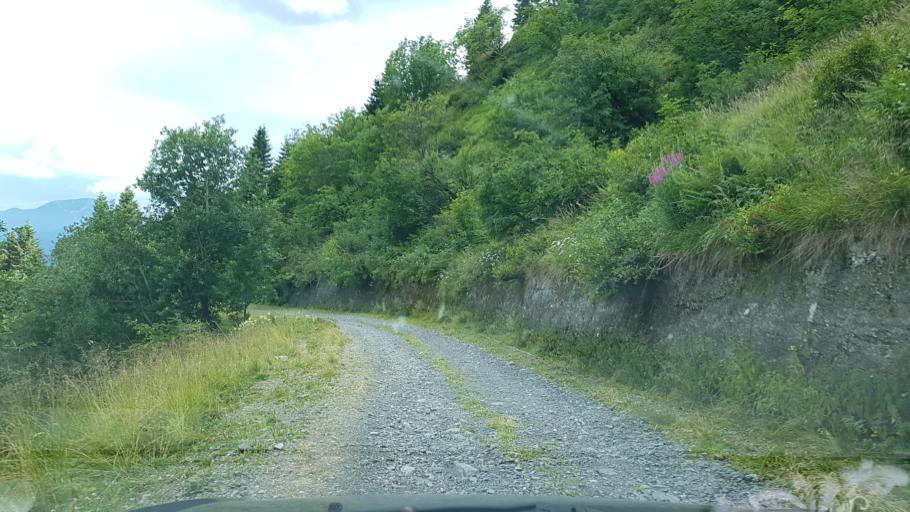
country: IT
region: Friuli Venezia Giulia
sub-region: Provincia di Udine
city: Cercivento
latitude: 46.5522
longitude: 12.9768
